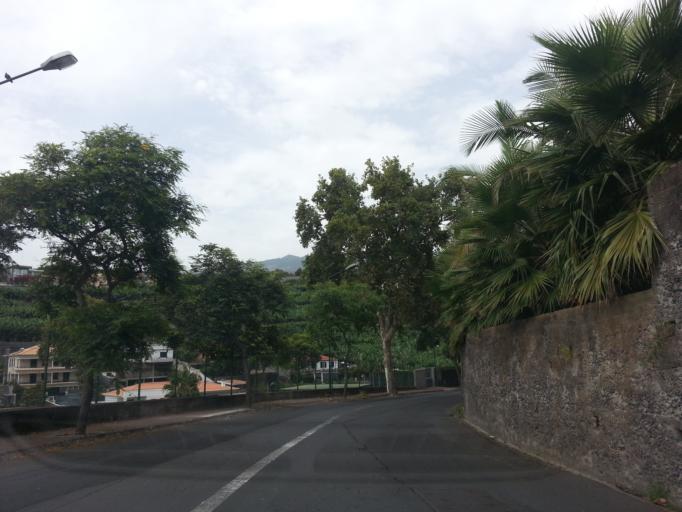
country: PT
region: Madeira
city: Camara de Lobos
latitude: 32.6445
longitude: -16.9609
